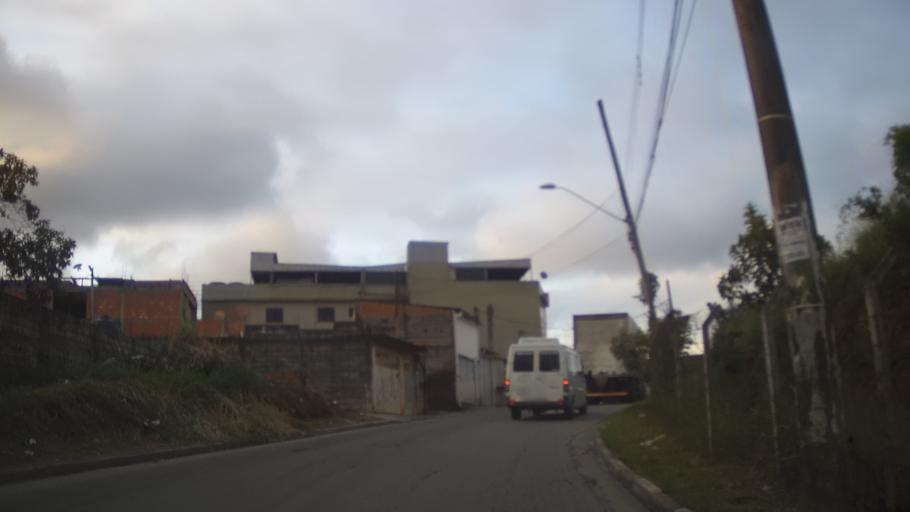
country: BR
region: Sao Paulo
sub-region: Itaquaquecetuba
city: Itaquaquecetuba
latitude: -23.4608
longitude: -46.4377
